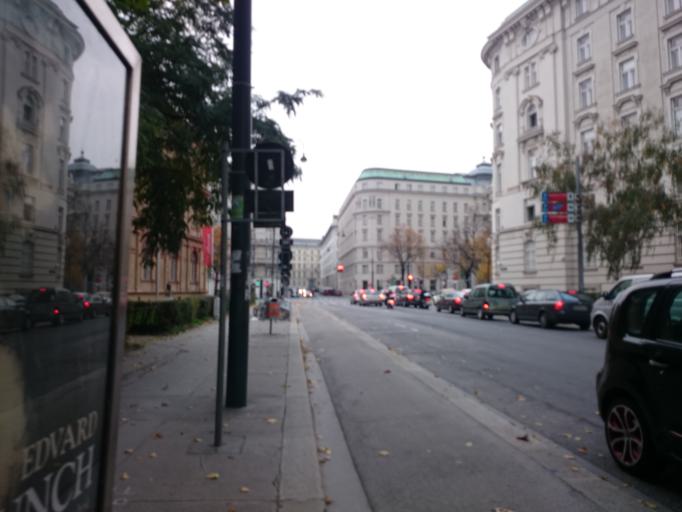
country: AT
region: Vienna
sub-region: Wien Stadt
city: Vienna
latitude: 48.2084
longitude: 16.3834
